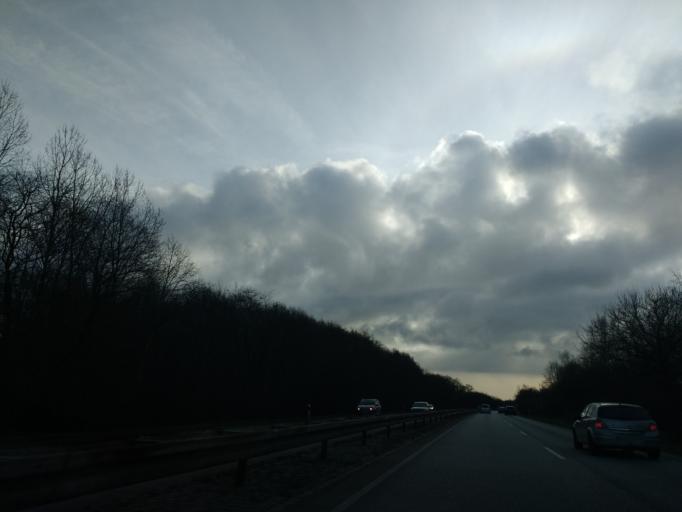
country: DE
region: Schleswig-Holstein
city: Neumunster
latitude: 54.1076
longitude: 9.9701
